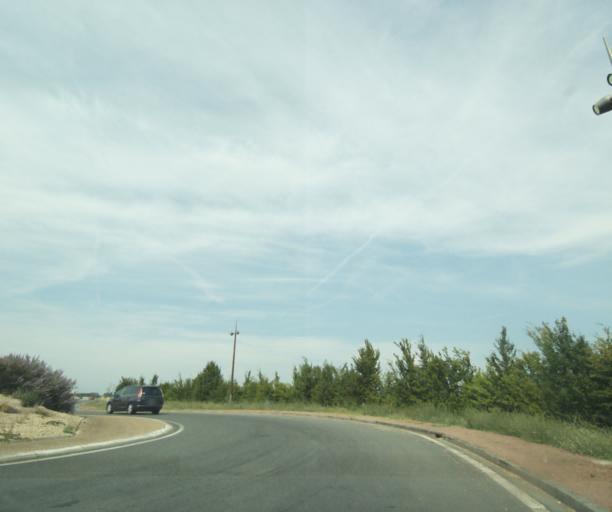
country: FR
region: Centre
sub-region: Departement d'Indre-et-Loire
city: Sorigny
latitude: 47.2564
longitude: 0.7007
